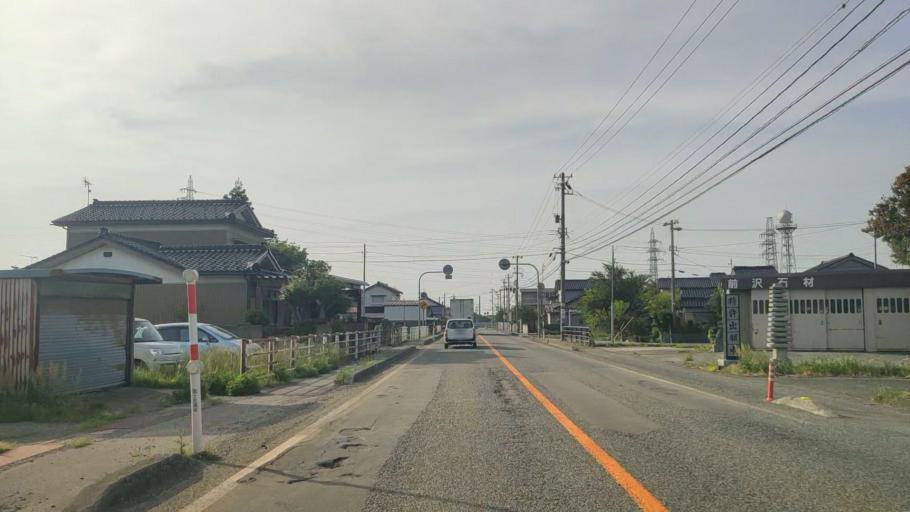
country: JP
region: Toyama
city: Yatsuomachi-higashikumisaka
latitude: 36.5641
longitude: 137.2126
